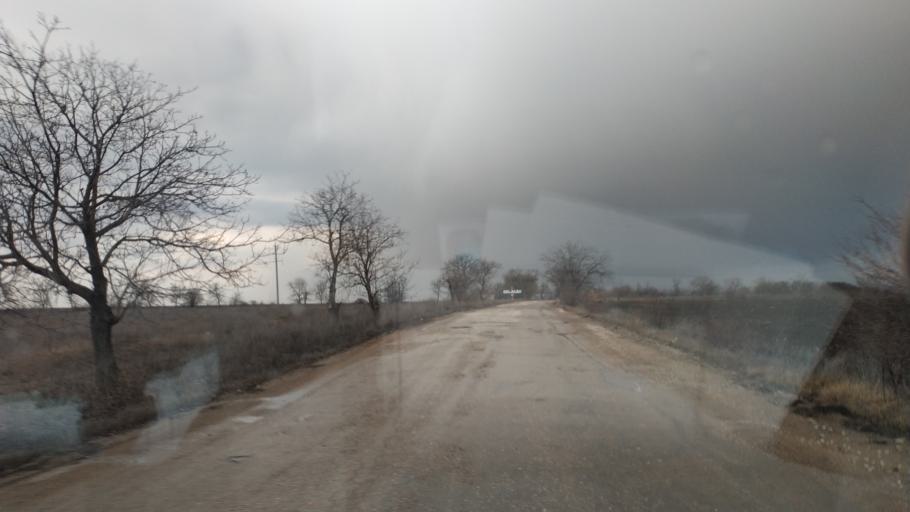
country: MD
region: Telenesti
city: Grigoriopol
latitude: 47.0669
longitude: 29.3002
